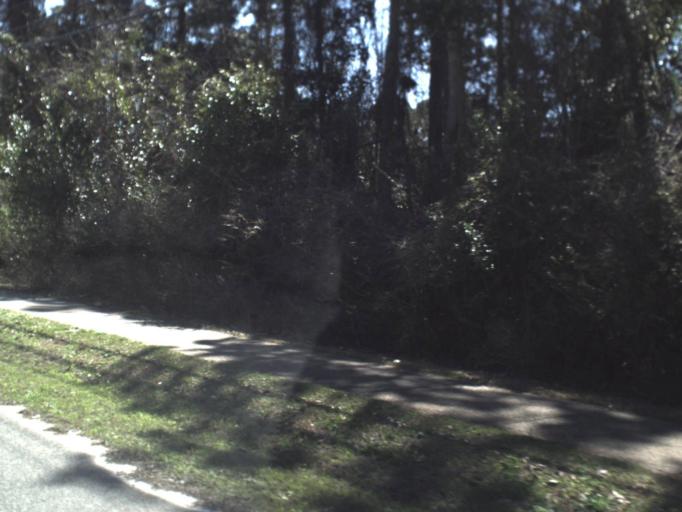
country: US
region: Florida
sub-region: Bay County
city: Pretty Bayou
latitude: 30.1885
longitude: -85.6765
